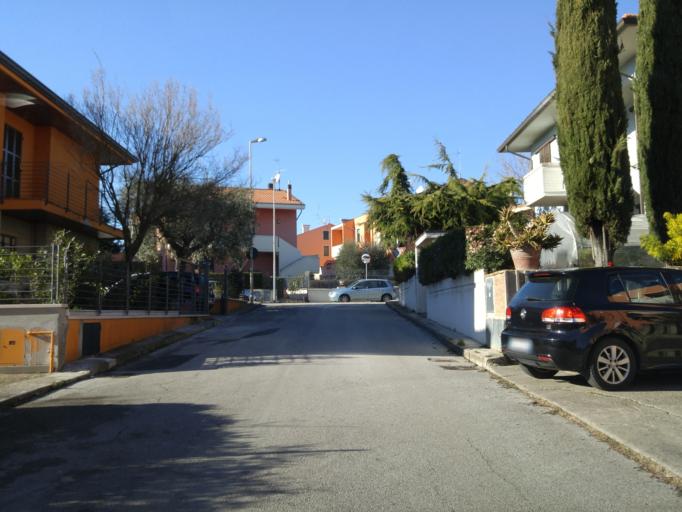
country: IT
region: The Marches
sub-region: Provincia di Pesaro e Urbino
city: Calcinelli
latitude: 43.7545
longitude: 12.9139
